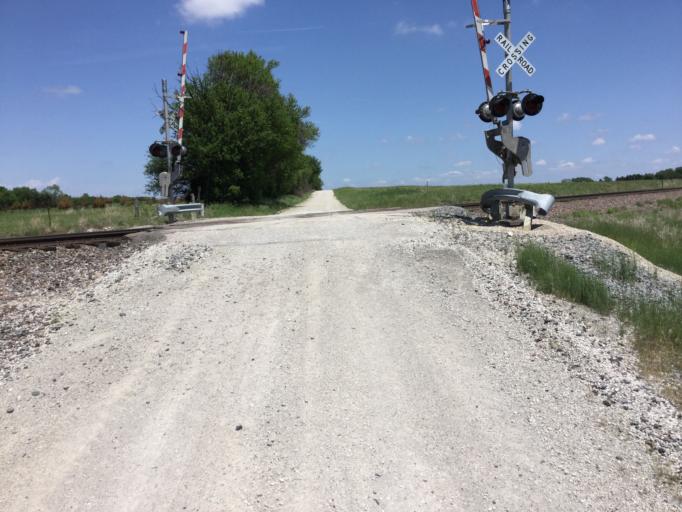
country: US
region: Kansas
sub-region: Coffey County
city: Burlington
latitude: 38.1655
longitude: -95.5363
